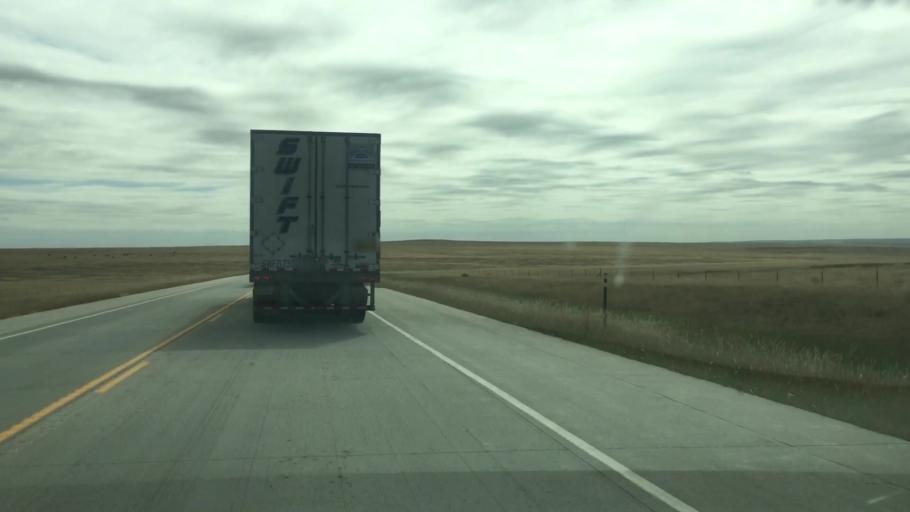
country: US
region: Colorado
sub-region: Lincoln County
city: Hugo
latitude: 38.9740
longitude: -103.2526
